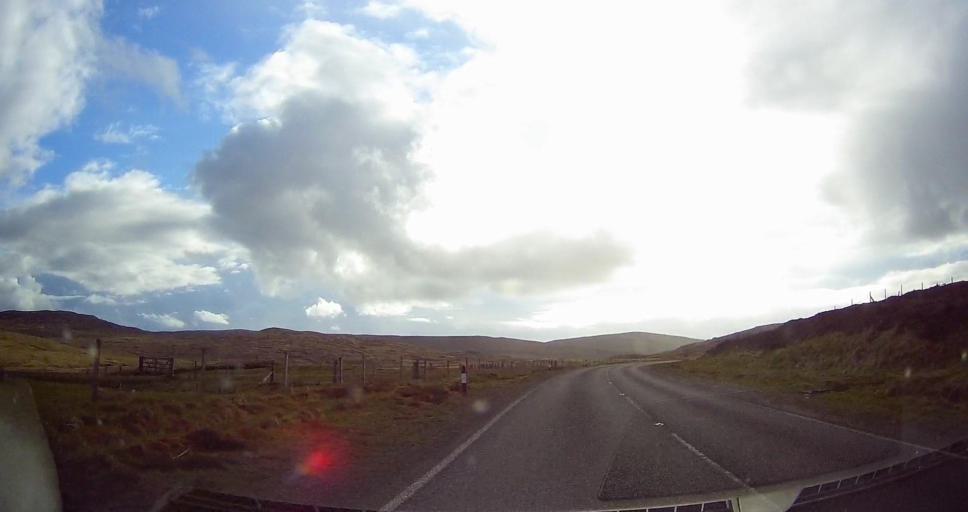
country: GB
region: Scotland
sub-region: Shetland Islands
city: Lerwick
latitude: 60.3486
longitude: -1.2235
